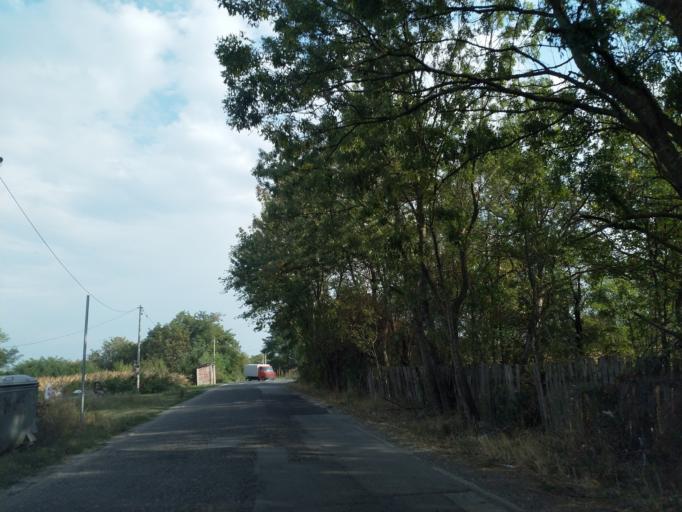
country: RS
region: Central Serbia
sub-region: Pomoravski Okrug
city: Paracin
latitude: 43.8444
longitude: 21.4700
